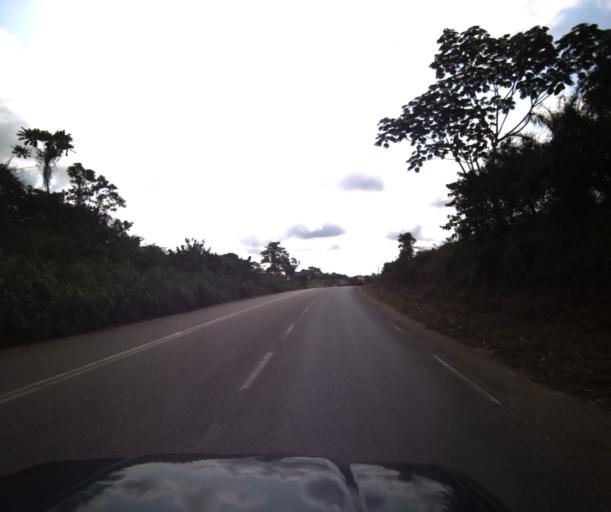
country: CM
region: Littoral
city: Edea
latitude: 3.7844
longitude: 10.1533
